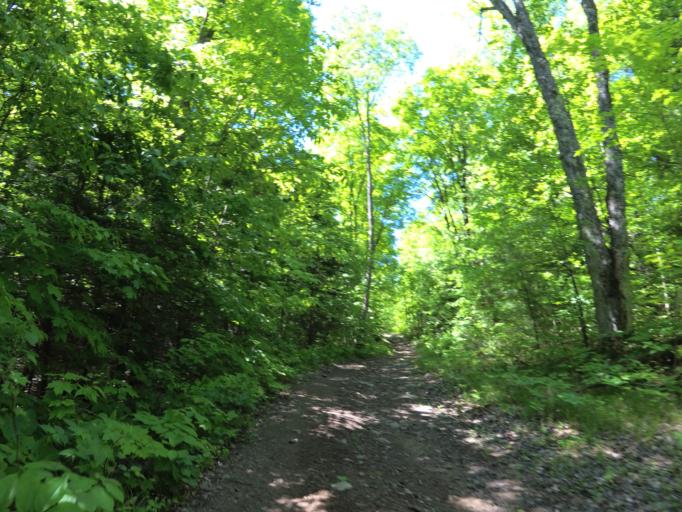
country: CA
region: Ontario
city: Renfrew
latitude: 45.0525
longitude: -77.0884
